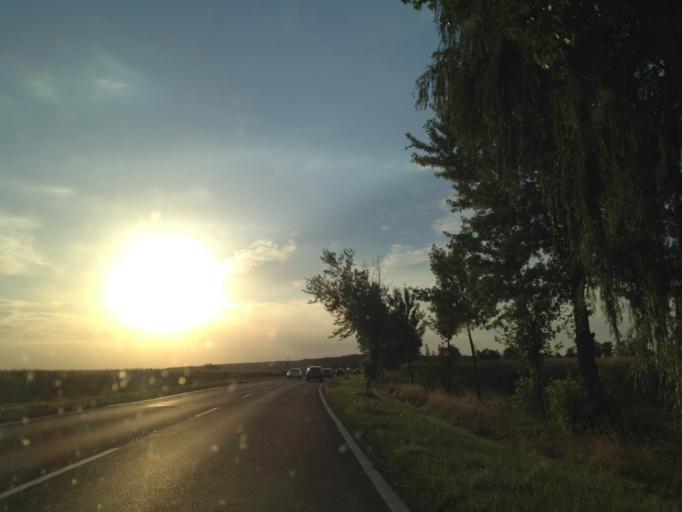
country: HU
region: Gyor-Moson-Sopron
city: Kimle
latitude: 47.8219
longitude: 17.3304
